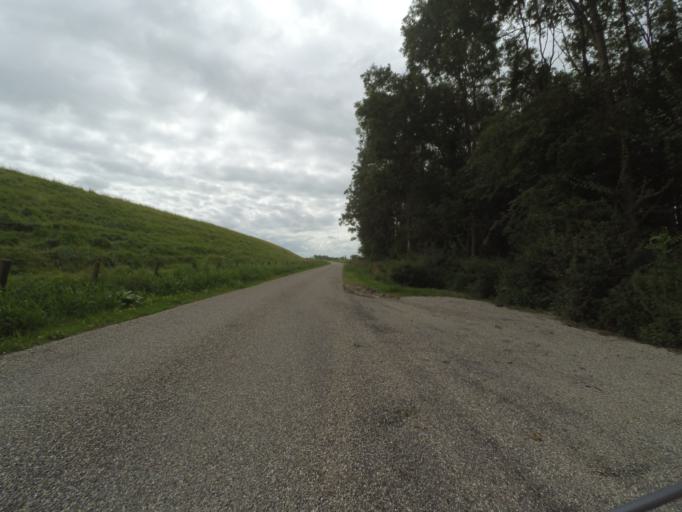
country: NL
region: Friesland
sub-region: Gemeente Dongeradeel
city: Anjum
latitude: 53.3554
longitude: 6.1450
